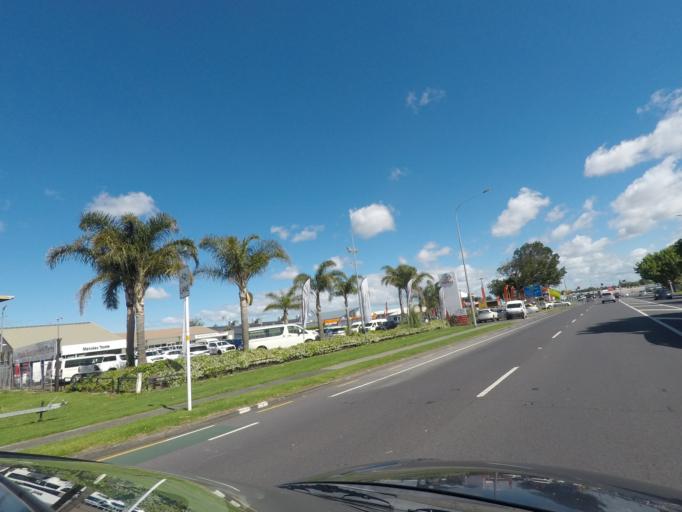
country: NZ
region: Auckland
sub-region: Auckland
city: Manukau City
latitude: -36.9834
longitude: 174.8786
